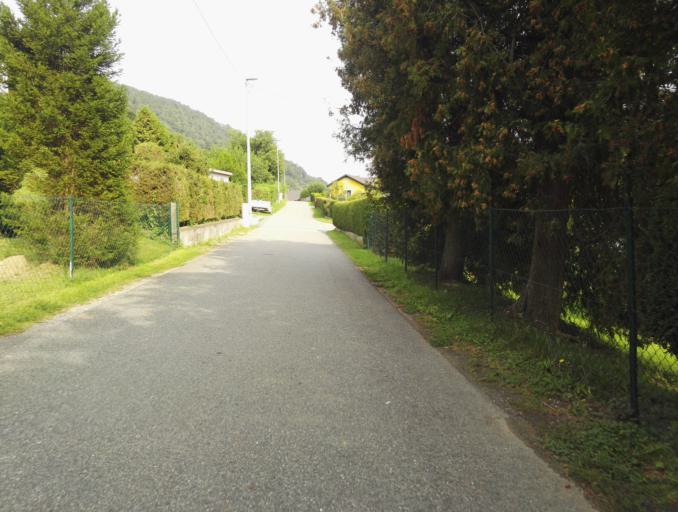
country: AT
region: Styria
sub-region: Graz Stadt
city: Goesting
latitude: 47.1090
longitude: 15.3739
